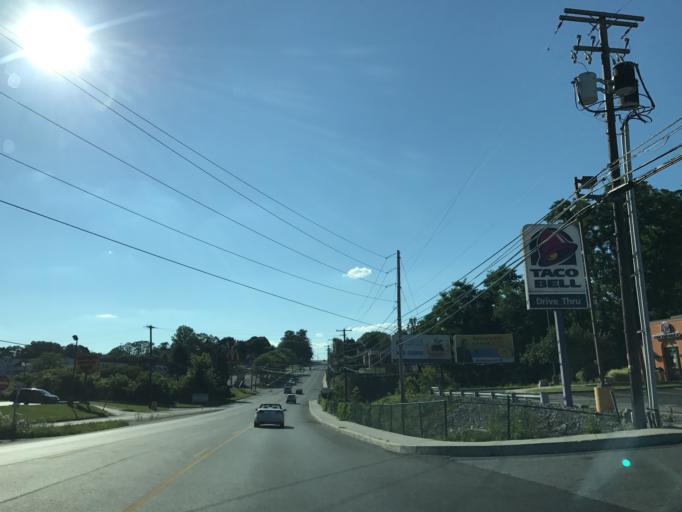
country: US
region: Pennsylvania
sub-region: Lancaster County
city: Rheems
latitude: 40.1390
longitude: -76.5876
